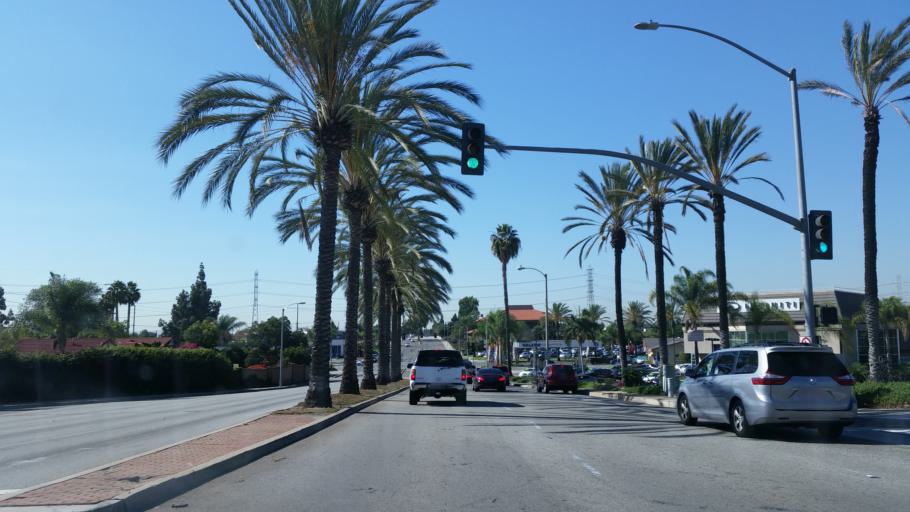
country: US
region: California
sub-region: Los Angeles County
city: Artesia
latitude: 33.8584
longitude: -118.0976
